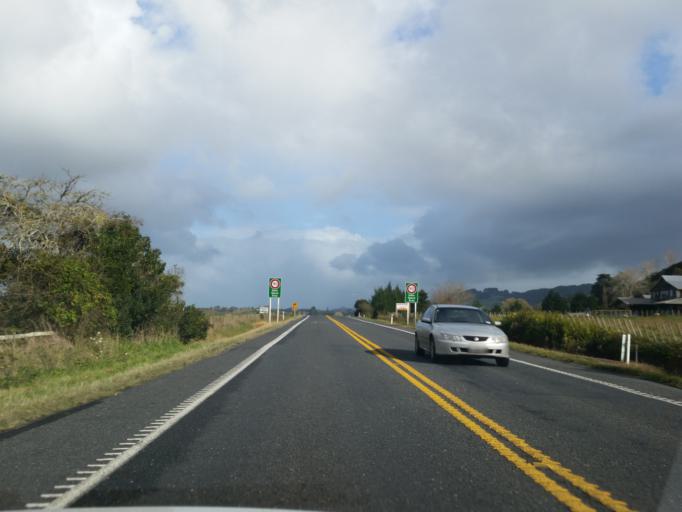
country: NZ
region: Auckland
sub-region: Auckland
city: Pukekohe East
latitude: -37.2135
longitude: 175.0714
